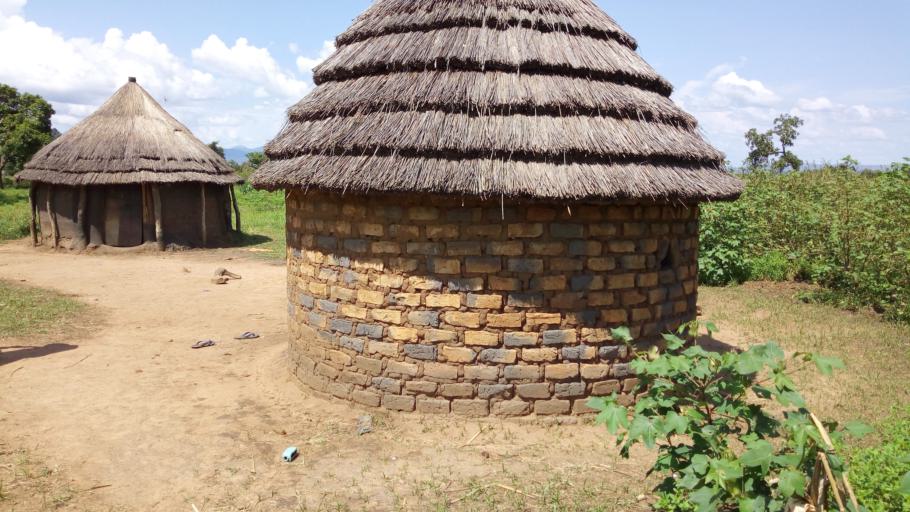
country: UG
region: Northern Region
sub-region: Adjumani District
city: Adjumani
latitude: 3.4597
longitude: 31.8990
